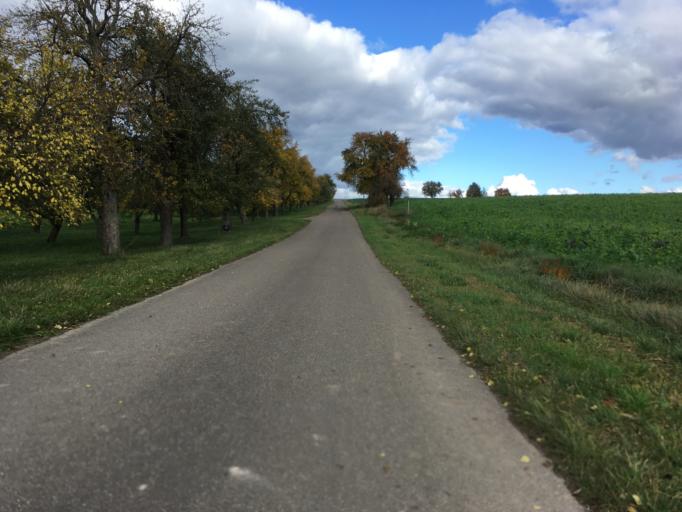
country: DE
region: Baden-Wuerttemberg
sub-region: Regierungsbezirk Stuttgart
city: Untermunkheim
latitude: 49.1831
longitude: 9.7084
